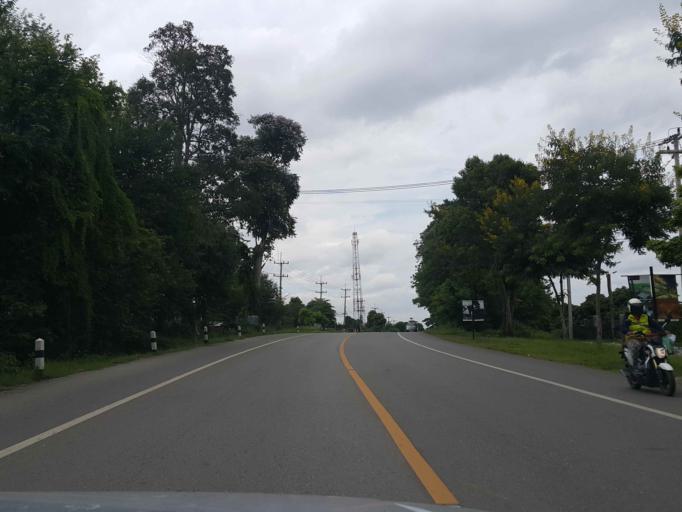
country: TH
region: Lamphun
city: Li
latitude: 17.7892
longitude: 98.9529
